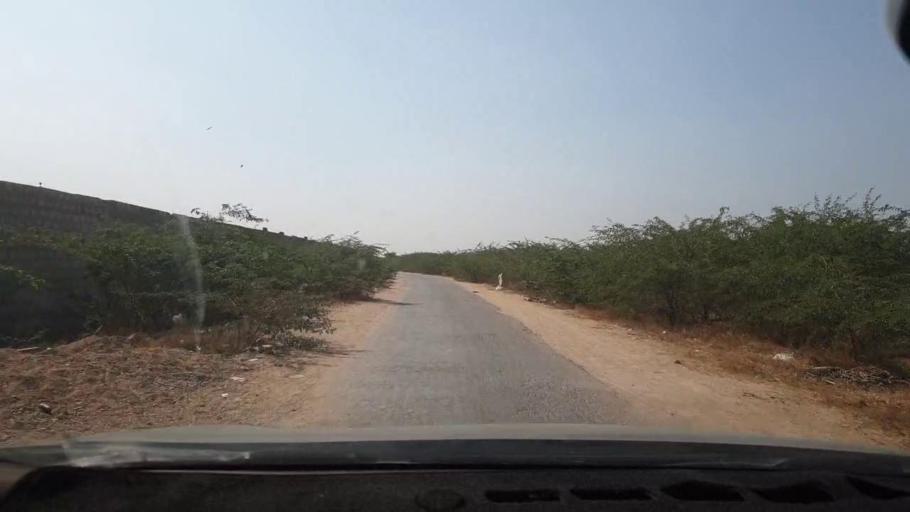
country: PK
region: Sindh
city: Malir Cantonment
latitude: 25.1300
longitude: 67.2294
